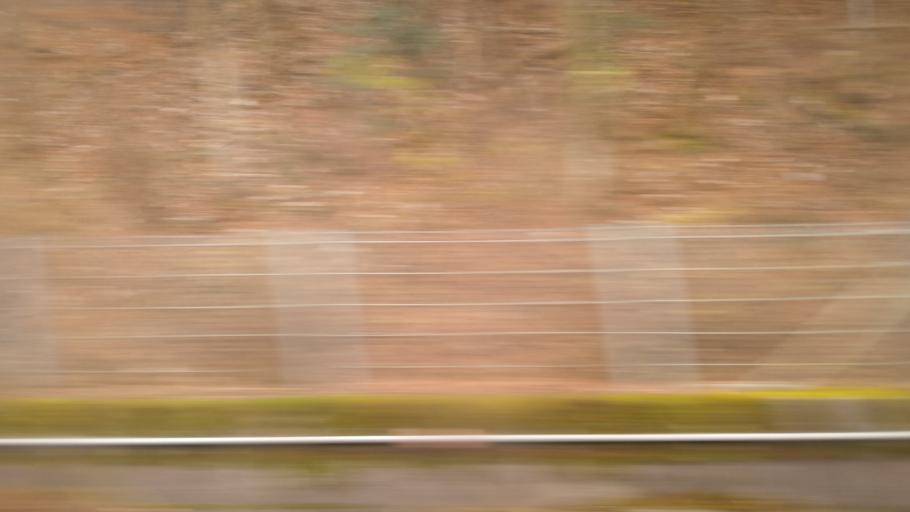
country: JP
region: Nagano
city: Ina
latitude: 35.8257
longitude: 137.6831
